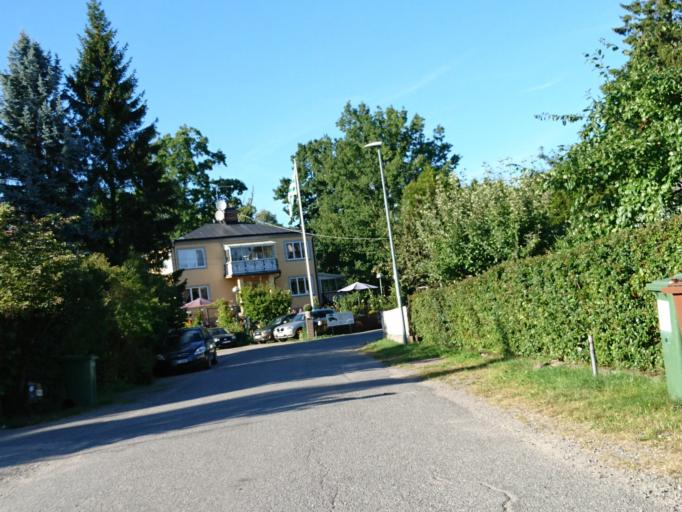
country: SE
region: Stockholm
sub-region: Huddinge Kommun
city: Segeltorp
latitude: 59.2753
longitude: 17.9306
